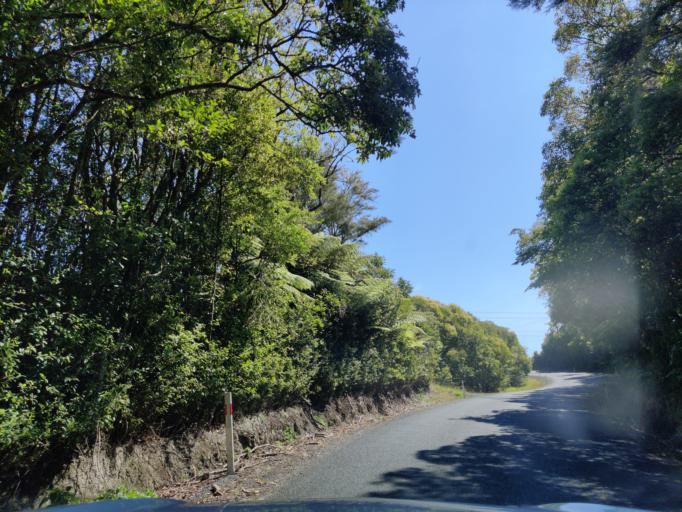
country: NZ
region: Auckland
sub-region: Auckland
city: Red Hill
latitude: -37.0659
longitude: 175.0763
